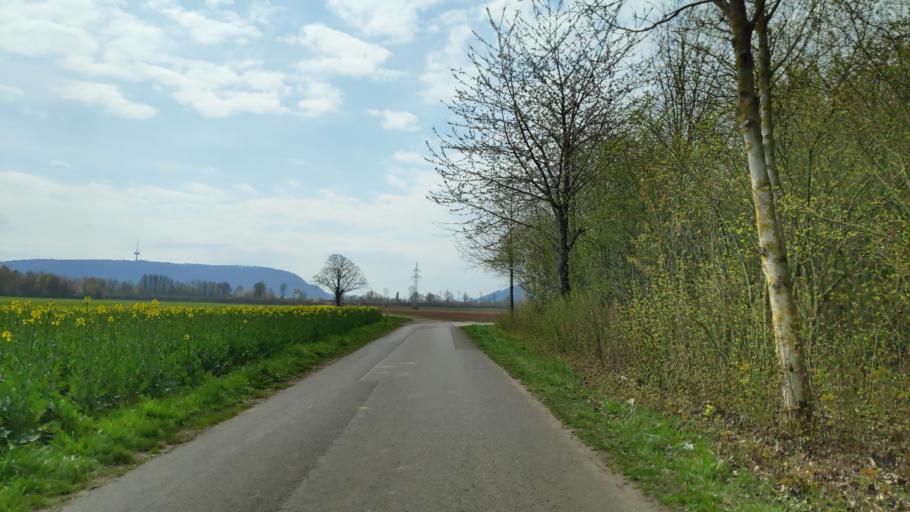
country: DE
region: North Rhine-Westphalia
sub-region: Regierungsbezirk Detmold
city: Minden
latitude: 52.2738
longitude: 8.9192
